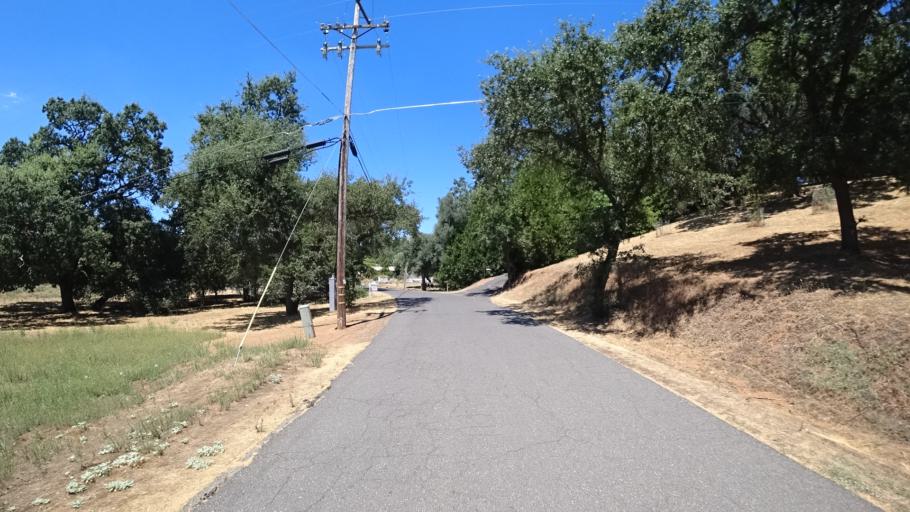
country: US
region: California
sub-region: Calaveras County
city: Murphys
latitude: 38.1310
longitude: -120.4372
